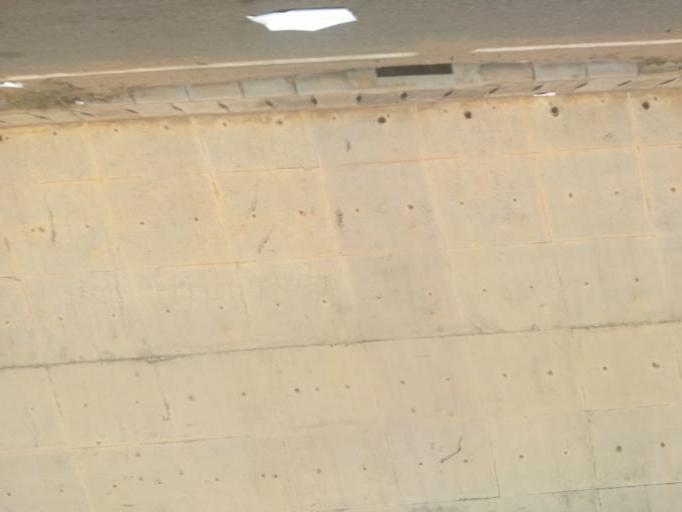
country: GH
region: Greater Accra
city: Dome
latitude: 5.6152
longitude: -0.2147
